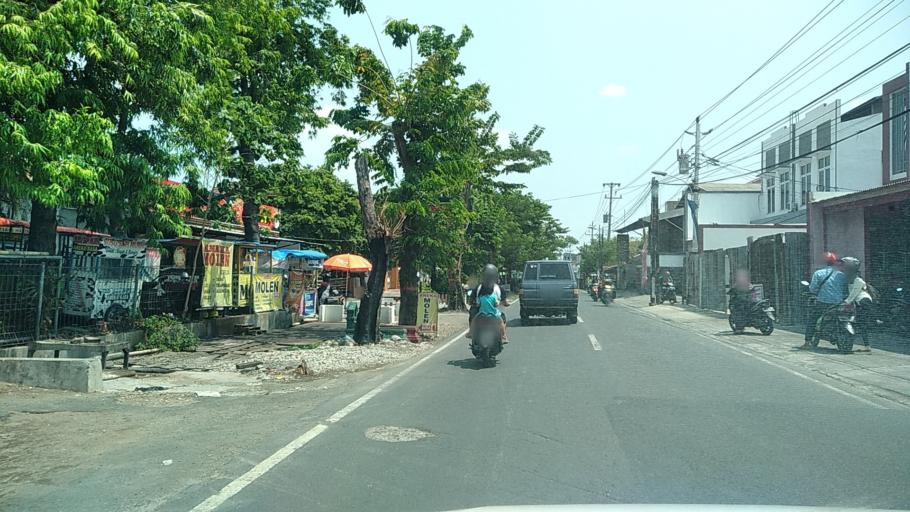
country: ID
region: Central Java
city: Semarang
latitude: -7.0099
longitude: 110.4420
